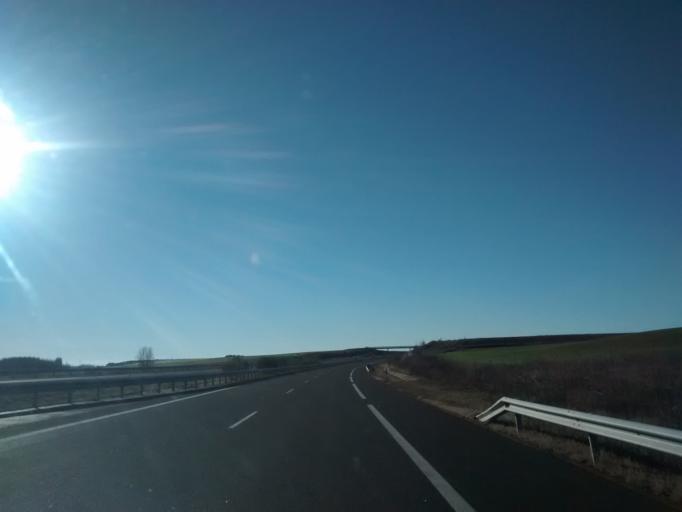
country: ES
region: Castille and Leon
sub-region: Provincia de Palencia
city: Espinosa de Villagonzalo
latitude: 42.4684
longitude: -4.3841
